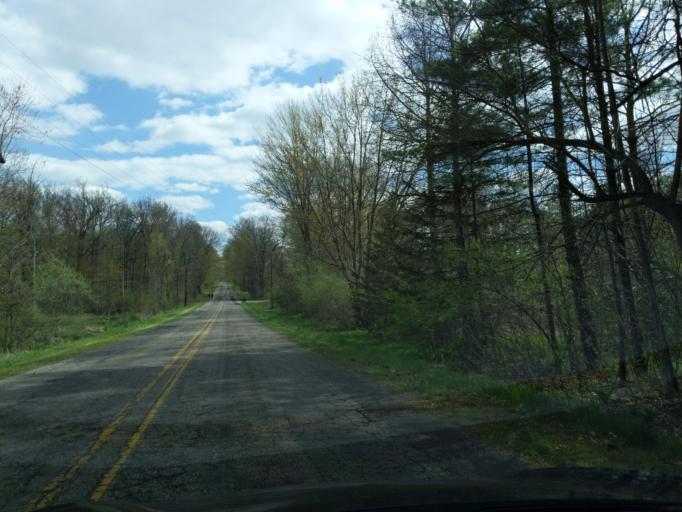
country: US
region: Michigan
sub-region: Ingham County
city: Leslie
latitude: 42.4057
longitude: -84.5269
